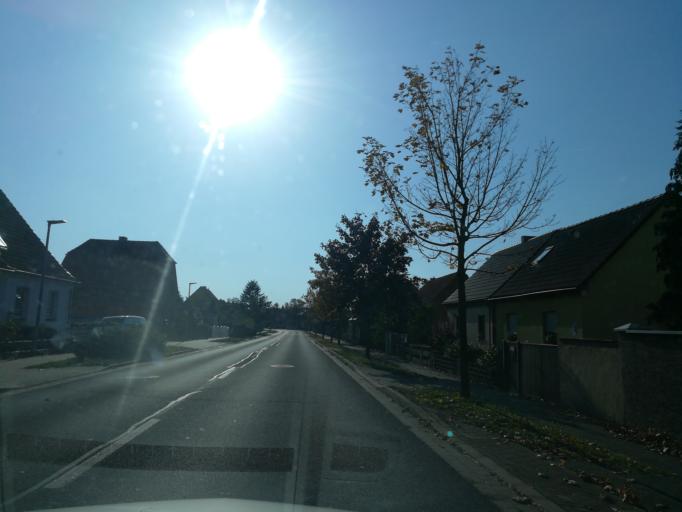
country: DE
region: Saxony-Anhalt
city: Wahlitz
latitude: 52.1185
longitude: 11.7646
